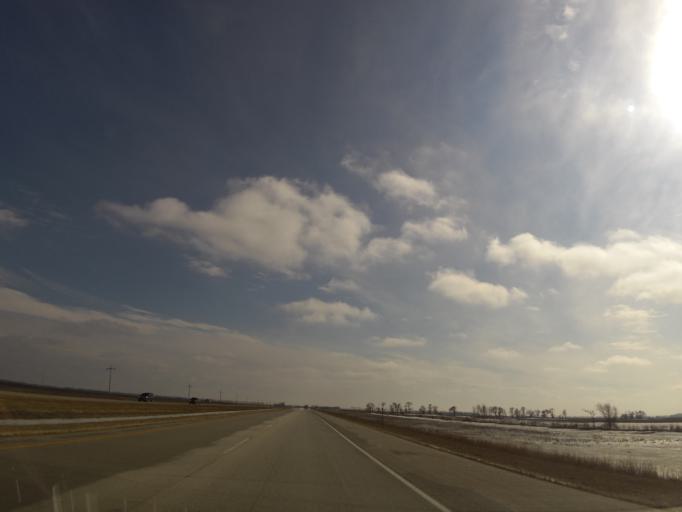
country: US
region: North Dakota
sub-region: Walsh County
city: Grafton
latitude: 48.3810
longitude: -97.1906
